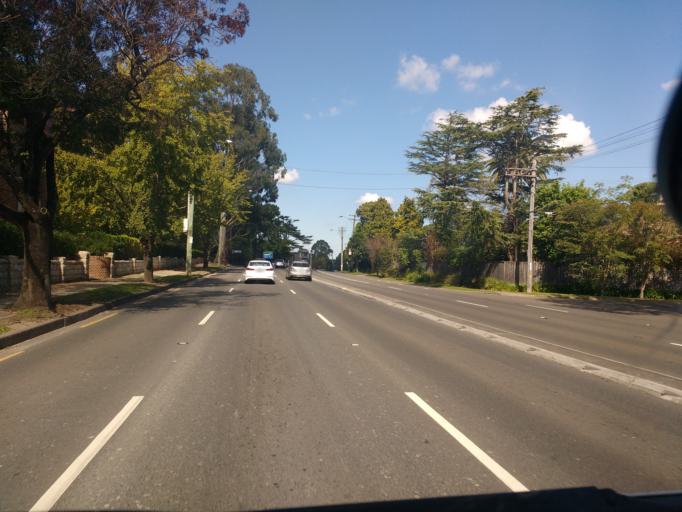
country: AU
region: New South Wales
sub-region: Ku-ring-gai
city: North Wahroonga
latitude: -33.7244
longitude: 151.1192
